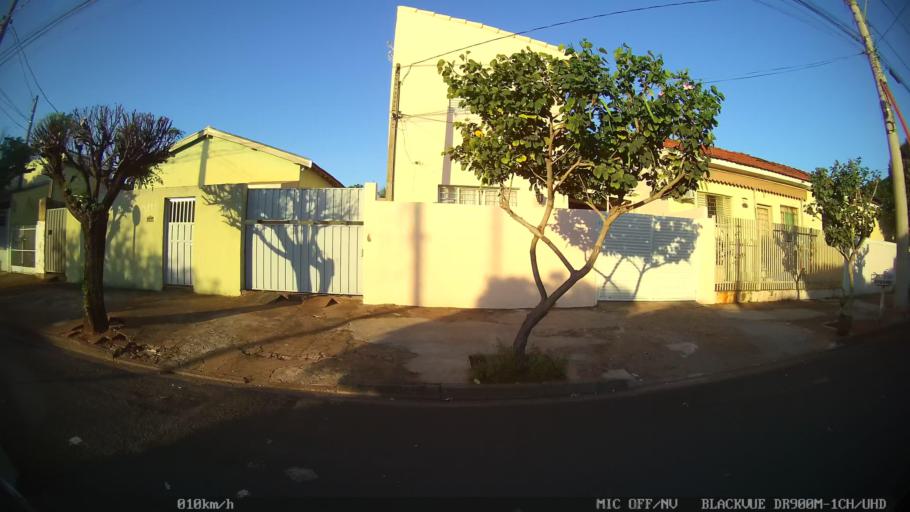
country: BR
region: Sao Paulo
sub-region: Sao Jose Do Rio Preto
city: Sao Jose do Rio Preto
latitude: -20.7899
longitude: -49.3709
